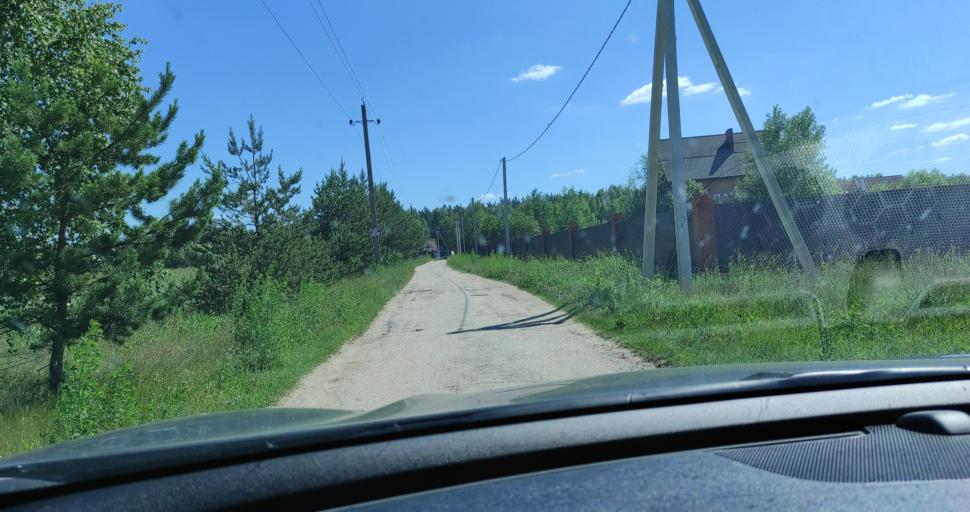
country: RU
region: Rjazan
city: Murmino
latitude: 54.5633
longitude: 40.0977
